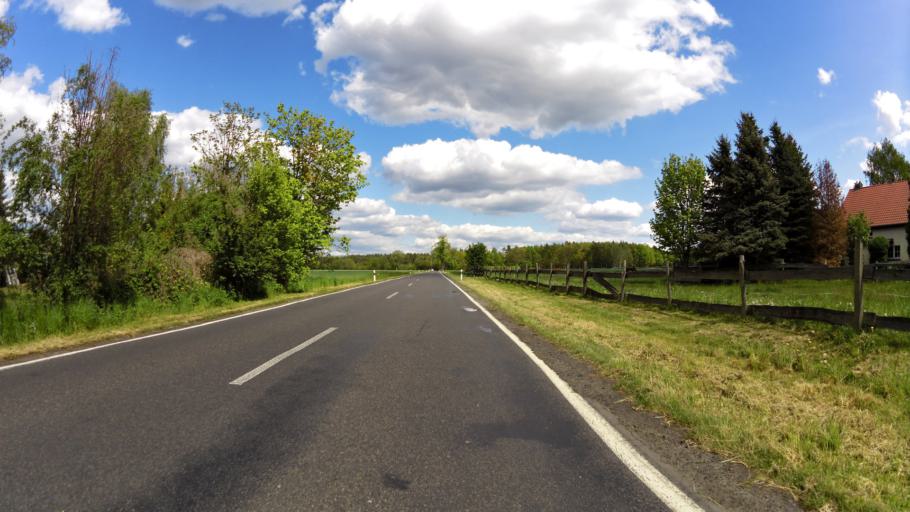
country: DE
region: Brandenburg
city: Diensdorf-Radlow
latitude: 52.1778
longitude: 14.0783
